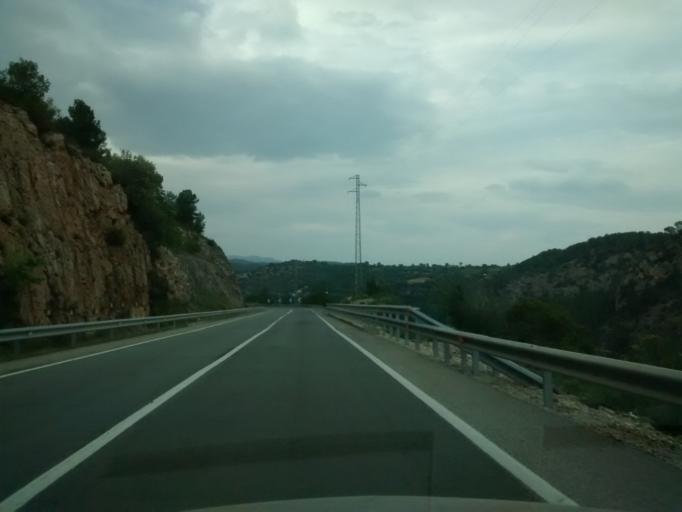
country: ES
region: Catalonia
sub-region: Provincia de Tarragona
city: Tivenys
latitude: 40.9393
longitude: 0.4887
